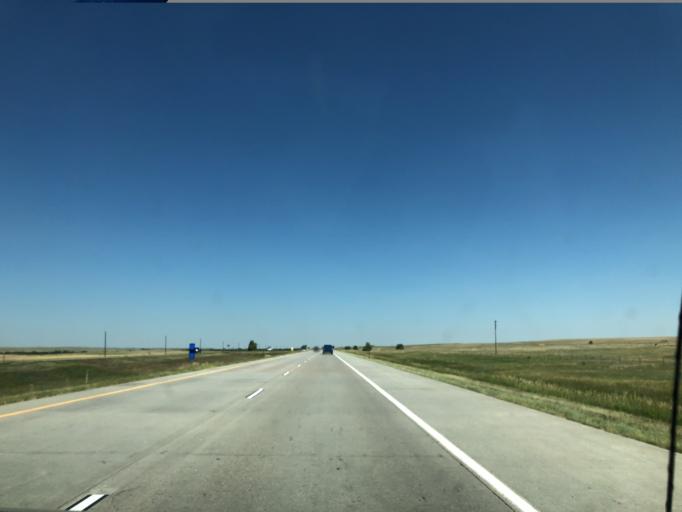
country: US
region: Colorado
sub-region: Arapahoe County
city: Byers
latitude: 39.5381
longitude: -103.9948
